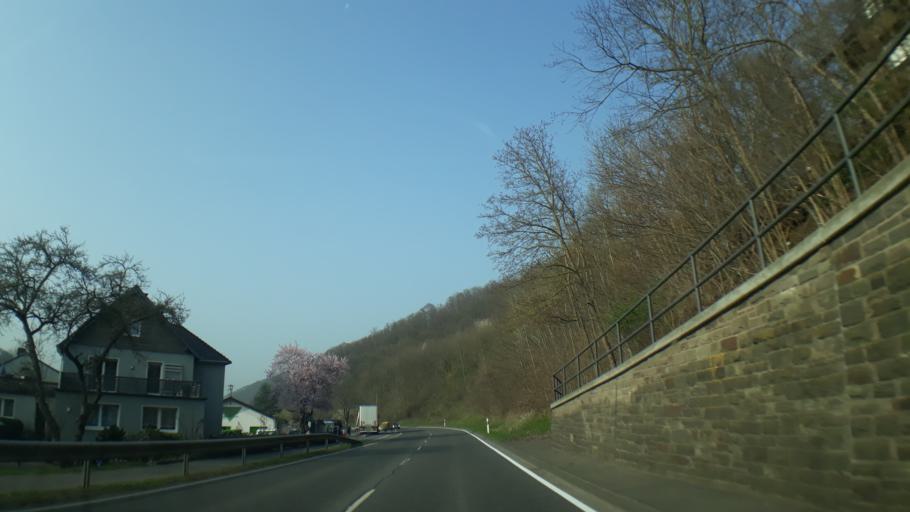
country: DE
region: North Rhine-Westphalia
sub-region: Regierungsbezirk Koln
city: Bad Munstereifel
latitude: 50.5348
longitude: 6.7697
